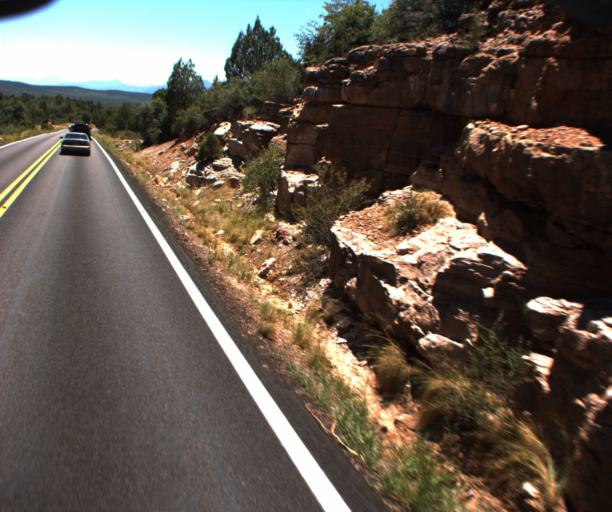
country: US
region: Arizona
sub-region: Gila County
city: Pine
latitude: 34.3532
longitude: -111.4251
